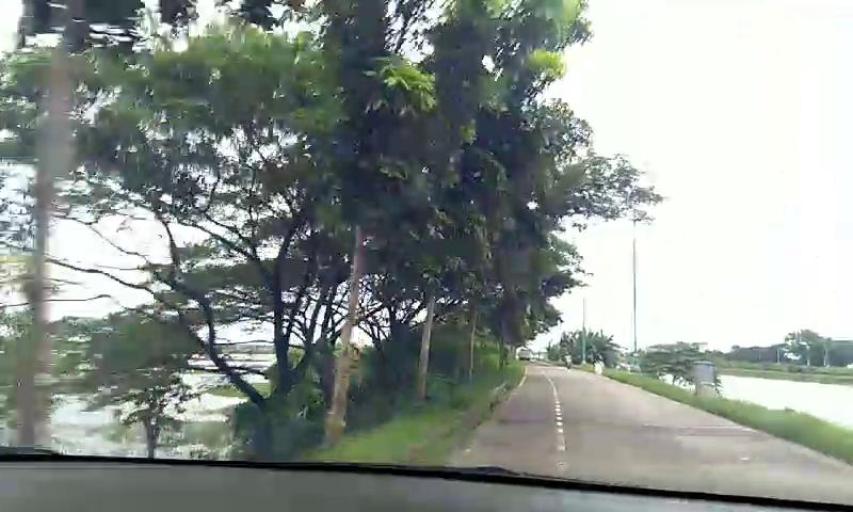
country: ID
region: West Java
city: Bekasi
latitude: -6.1270
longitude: 106.9692
